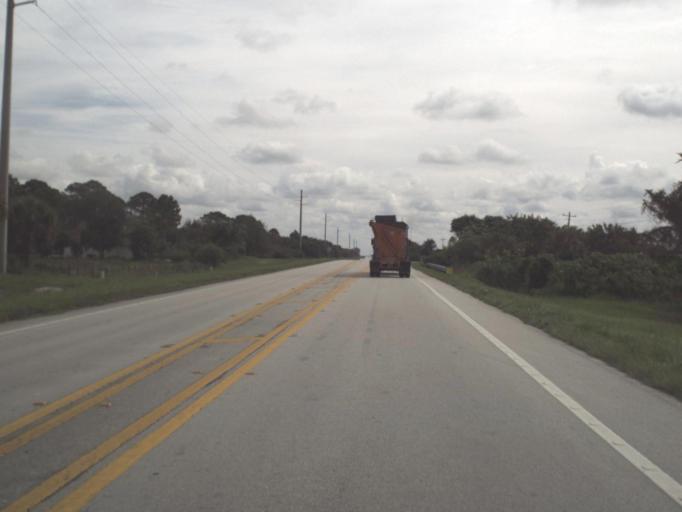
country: US
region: Florida
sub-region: Highlands County
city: Lake Placid
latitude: 27.2083
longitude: -81.3158
